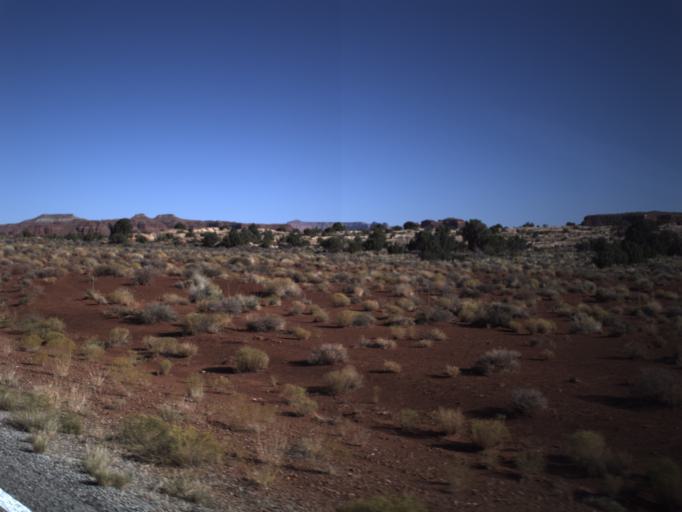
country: US
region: Utah
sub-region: San Juan County
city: Blanding
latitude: 37.7991
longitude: -110.3057
